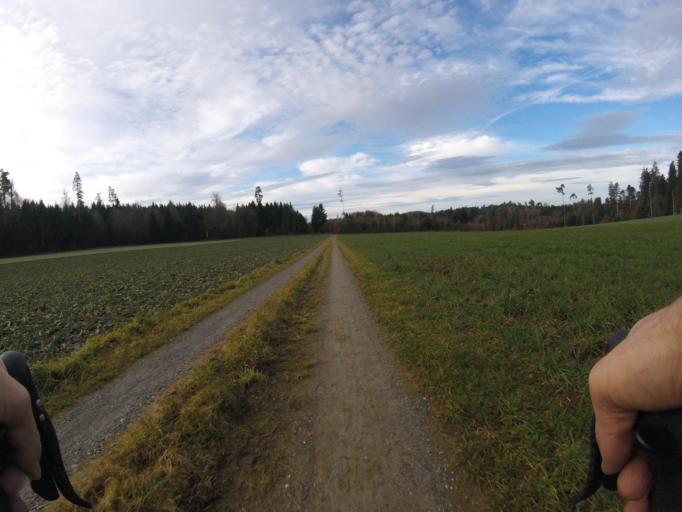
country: CH
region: Fribourg
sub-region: Sense District
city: Flamatt
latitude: 46.9122
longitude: 7.3439
